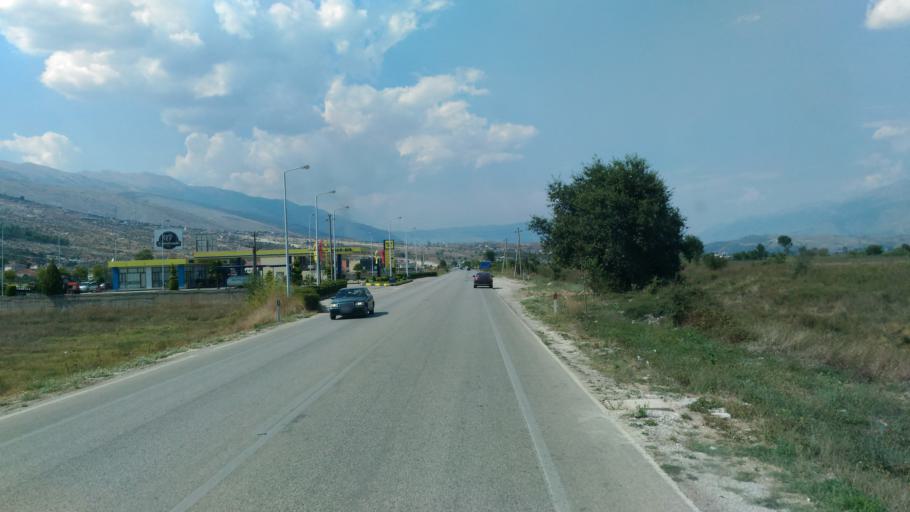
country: AL
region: Gjirokaster
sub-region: Rrethi i Gjirokastres
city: Dervician
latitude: 40.0298
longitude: 20.1857
